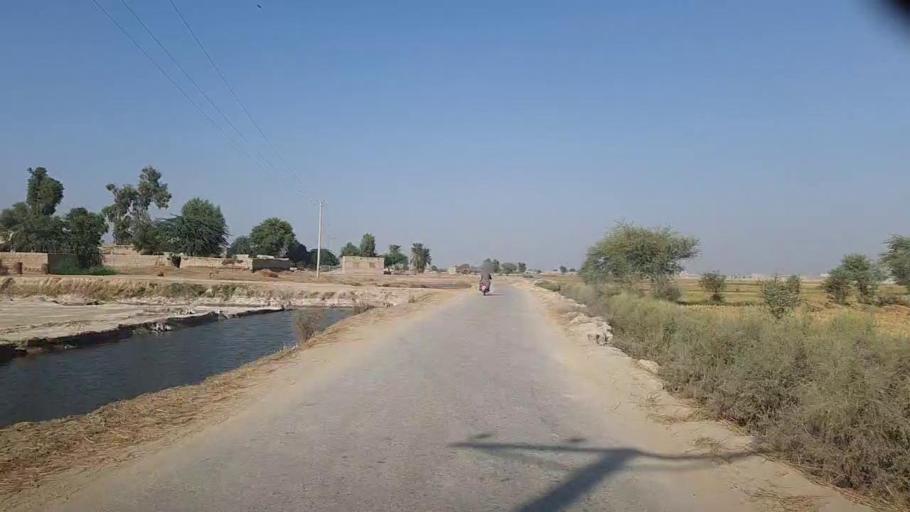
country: PK
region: Sindh
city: Tangwani
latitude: 28.2541
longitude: 68.9960
